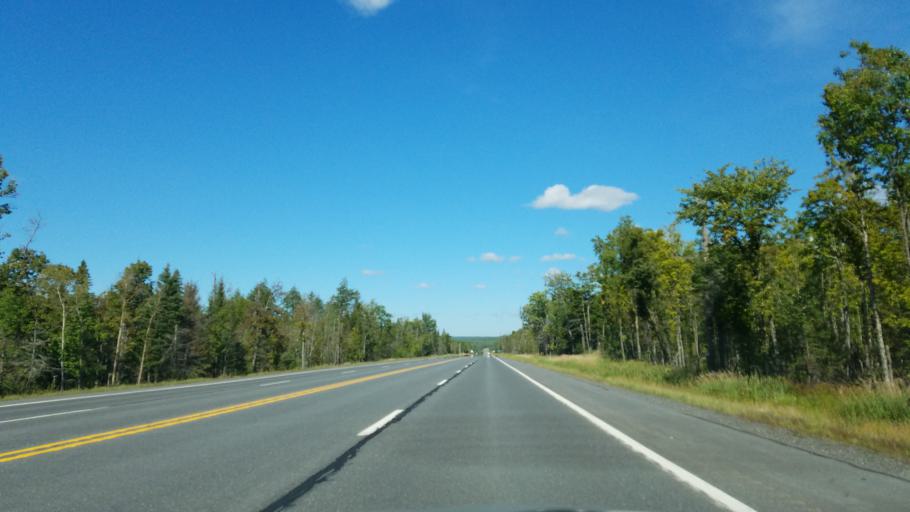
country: US
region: Michigan
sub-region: Baraga County
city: L'Anse
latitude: 46.5595
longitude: -88.5112
